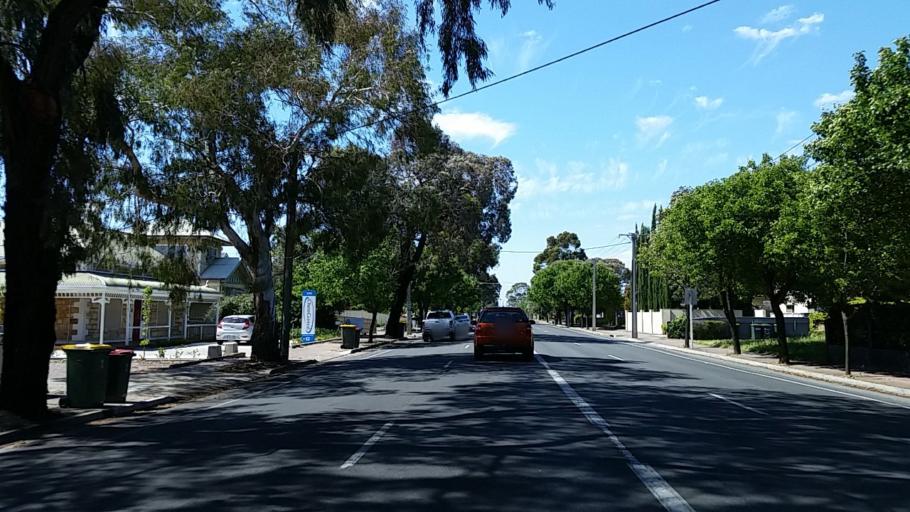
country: AU
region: South Australia
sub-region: Norwood Payneham St Peters
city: Royston Park
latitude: -34.9049
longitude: 138.6318
